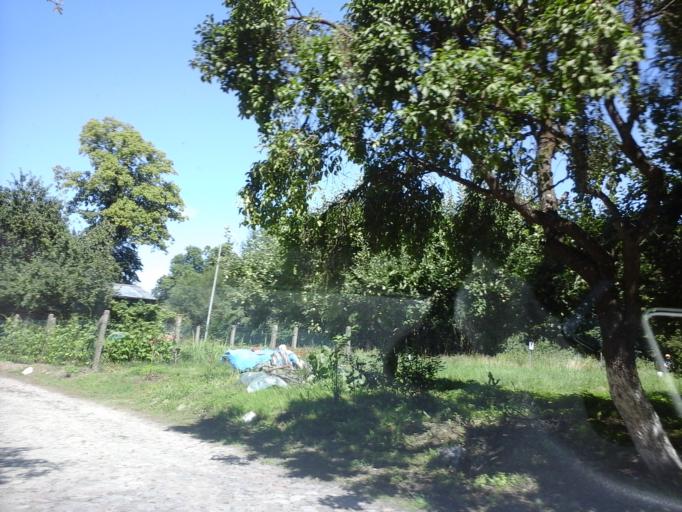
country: PL
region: West Pomeranian Voivodeship
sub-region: Powiat choszczenski
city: Recz
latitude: 53.2932
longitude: 15.5061
